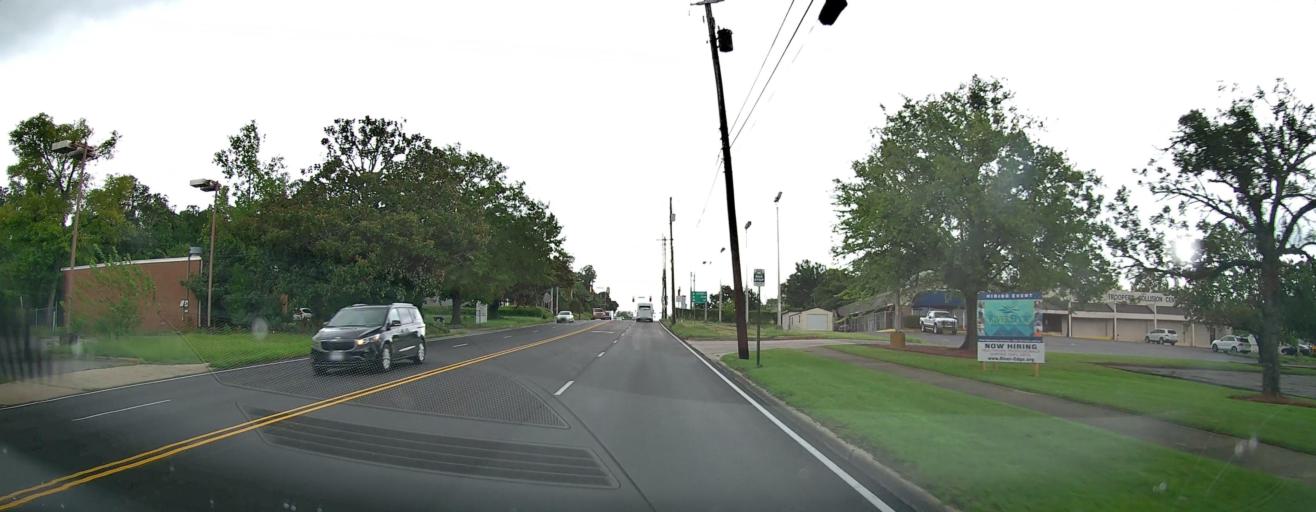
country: US
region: Georgia
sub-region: Bibb County
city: Macon
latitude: 32.8482
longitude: -83.6225
